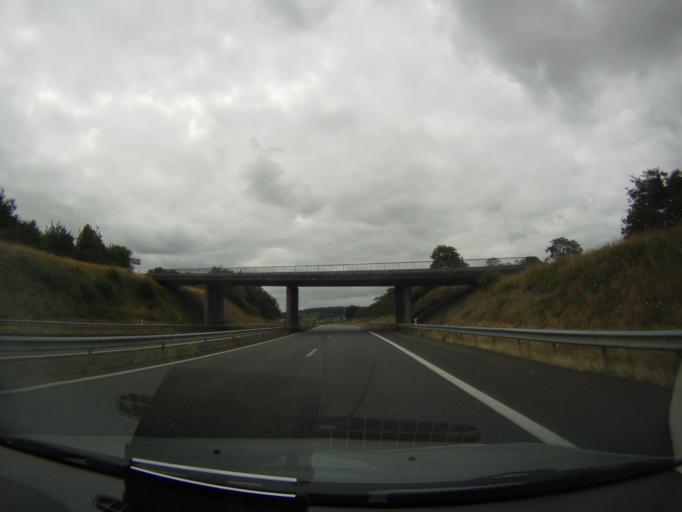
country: FR
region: Brittany
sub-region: Departement d'Ille-et-Vilaine
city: Pance
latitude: 47.8899
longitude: -1.6896
